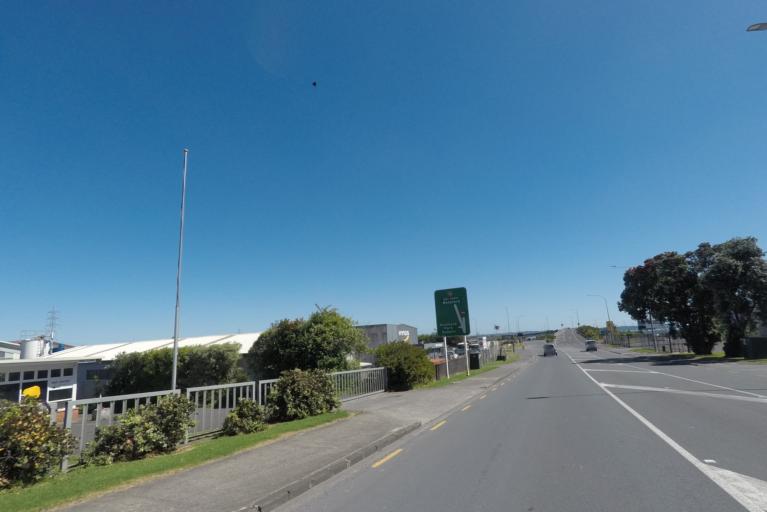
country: NZ
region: Auckland
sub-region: Auckland
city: Rosebank
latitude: -36.8682
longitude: 174.6663
